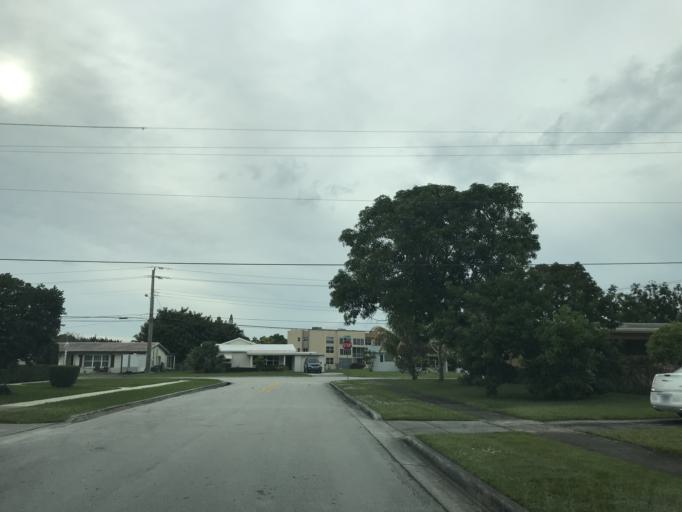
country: US
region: Florida
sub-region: Broward County
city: Margate
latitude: 26.2521
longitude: -80.2114
